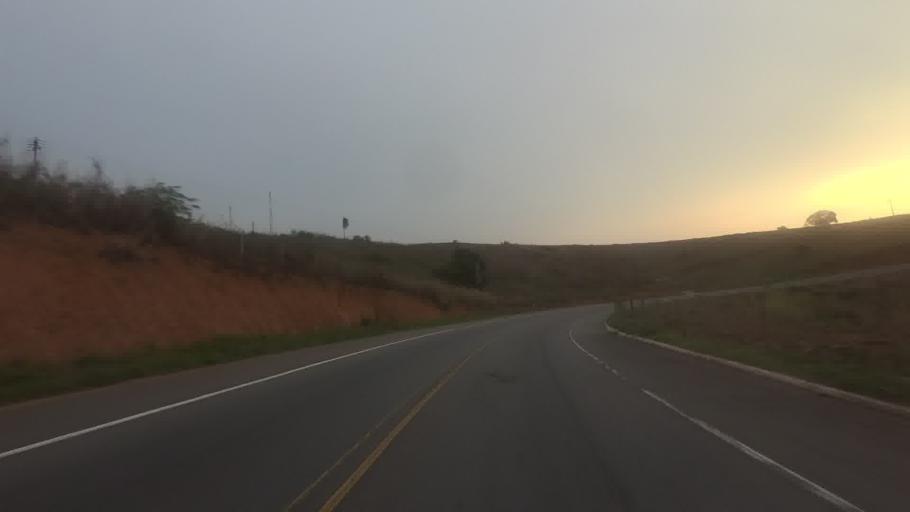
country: BR
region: Minas Gerais
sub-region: Recreio
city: Recreio
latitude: -21.7477
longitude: -42.4652
